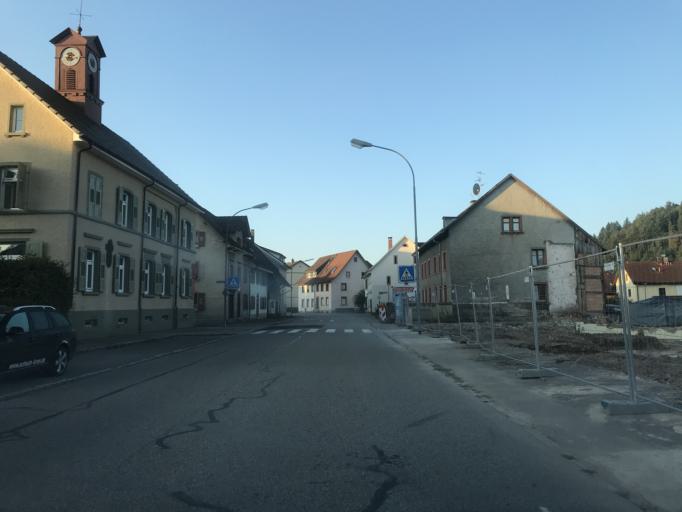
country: DE
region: Baden-Wuerttemberg
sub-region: Freiburg Region
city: Schopfheim
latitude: 47.6606
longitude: 7.8345
